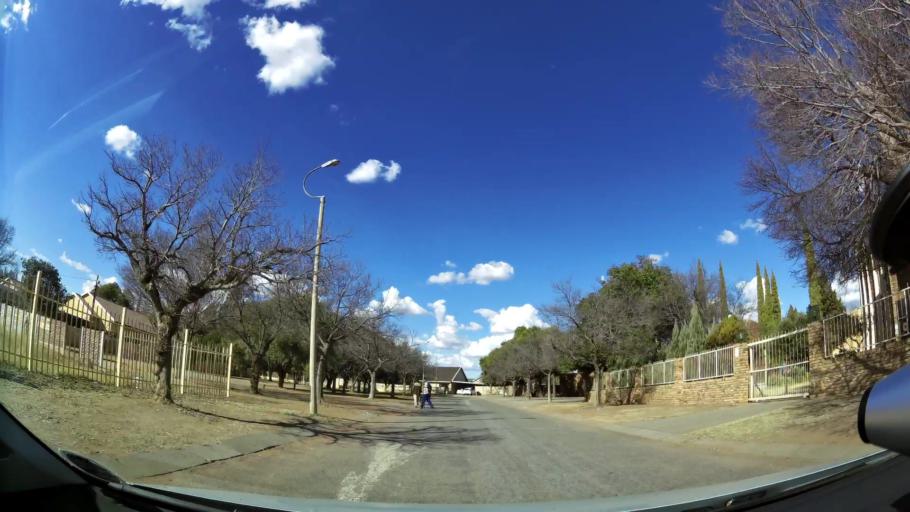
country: ZA
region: North-West
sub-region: Dr Kenneth Kaunda District Municipality
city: Klerksdorp
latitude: -26.8607
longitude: 26.6372
